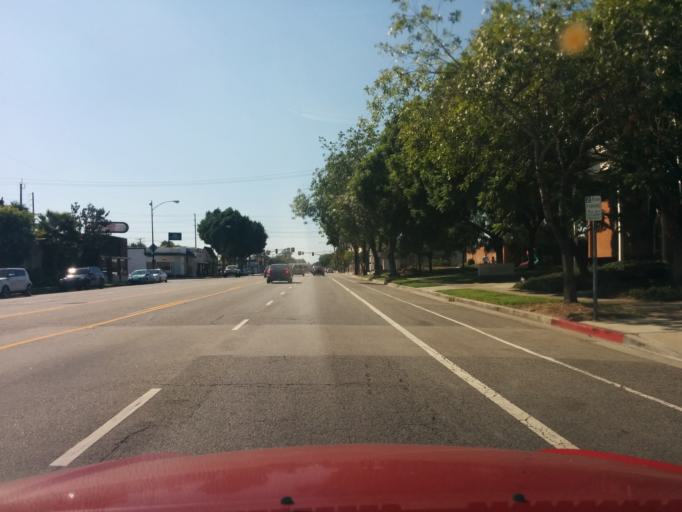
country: US
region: California
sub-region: Los Angeles County
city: North Hollywood
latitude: 34.1848
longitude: -118.3470
